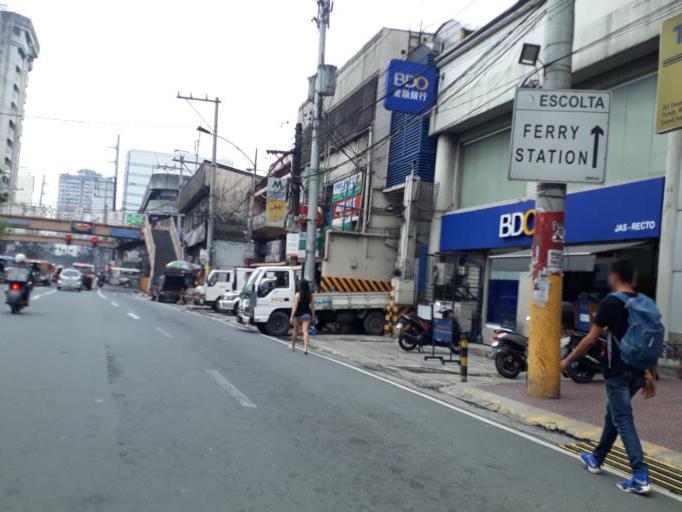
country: PH
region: Metro Manila
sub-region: City of Manila
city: Manila
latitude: 14.6069
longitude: 120.9751
